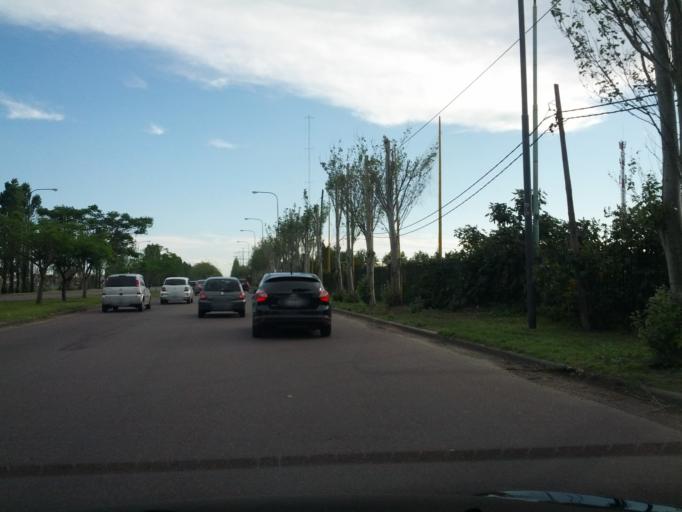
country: AR
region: Buenos Aires F.D.
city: Villa Lugano
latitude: -34.6833
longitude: -58.4432
